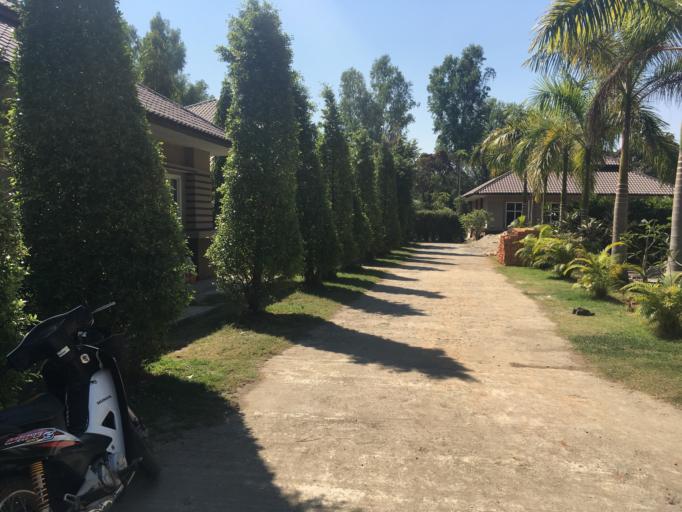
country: MM
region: Kayin
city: Hpa-an
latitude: 16.8896
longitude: 97.6750
